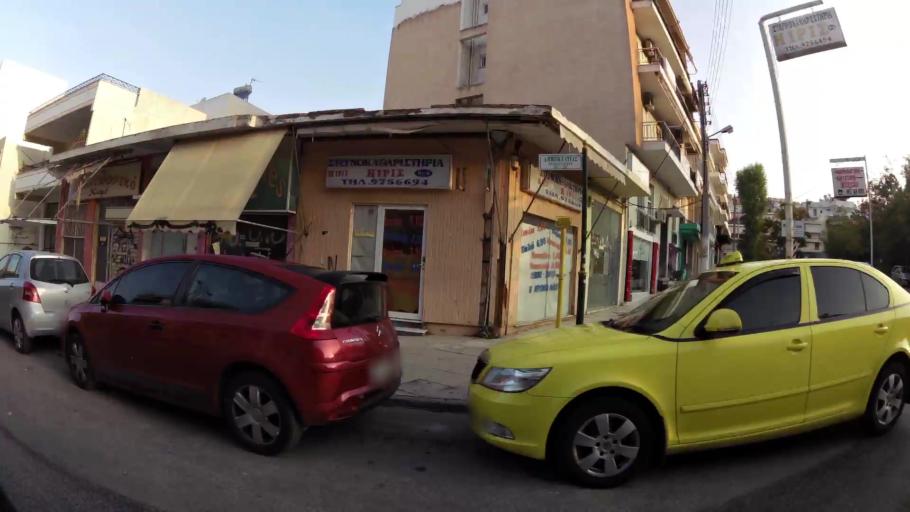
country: GR
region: Attica
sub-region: Nomarchia Athinas
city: Ymittos
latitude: 37.9463
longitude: 23.7544
